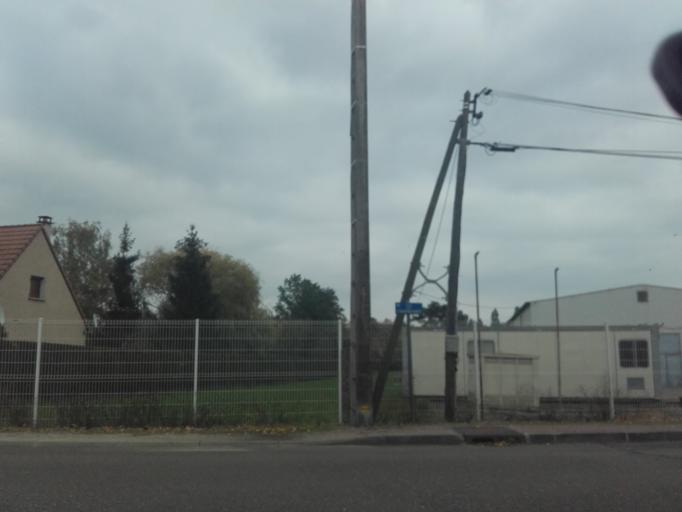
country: FR
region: Bourgogne
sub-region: Departement de Saone-et-Loire
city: Chagny
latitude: 46.8988
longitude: 4.7590
